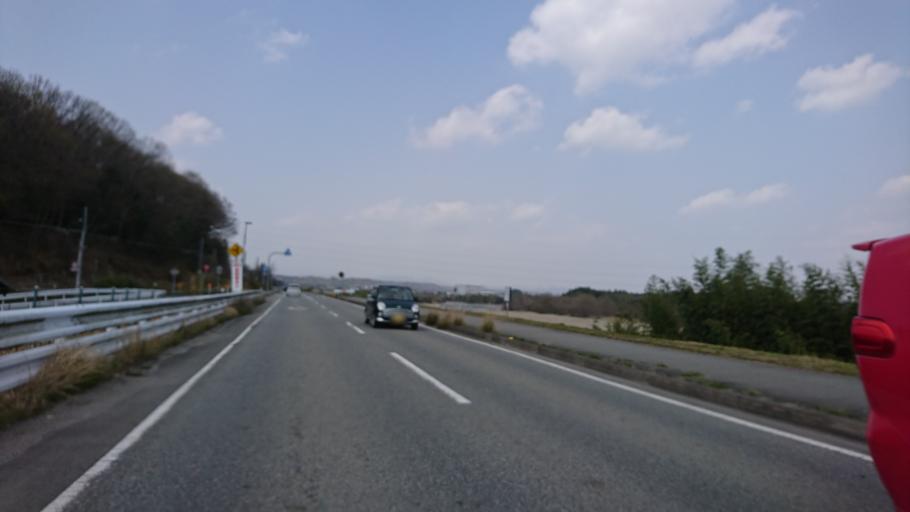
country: JP
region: Hyogo
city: Ono
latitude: 34.8432
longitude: 134.9115
